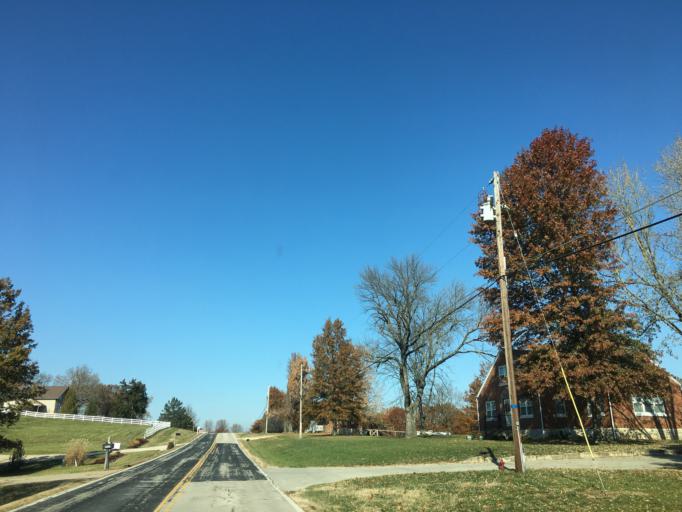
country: US
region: Missouri
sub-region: Cole County
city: Wardsville
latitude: 38.4684
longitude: -92.1762
